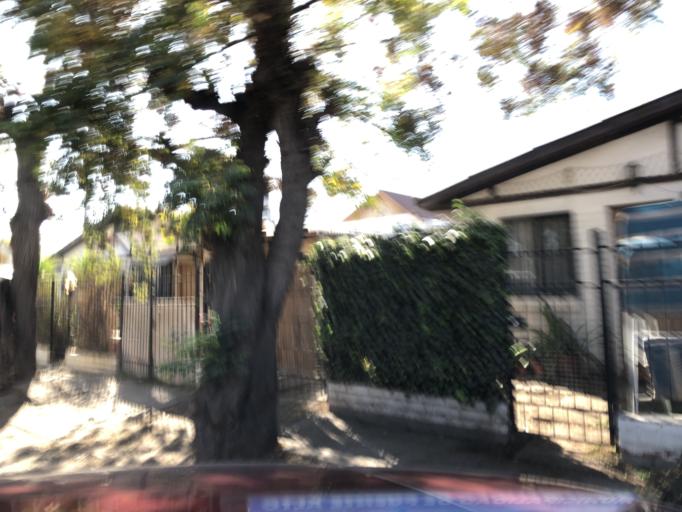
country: CL
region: Santiago Metropolitan
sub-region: Provincia de Cordillera
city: Puente Alto
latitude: -33.5718
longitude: -70.5795
